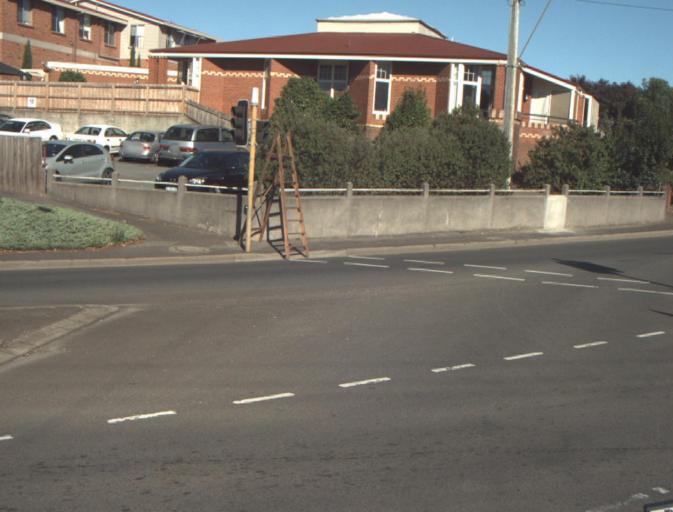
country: AU
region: Tasmania
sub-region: Launceston
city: East Launceston
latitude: -41.4598
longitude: 147.1557
